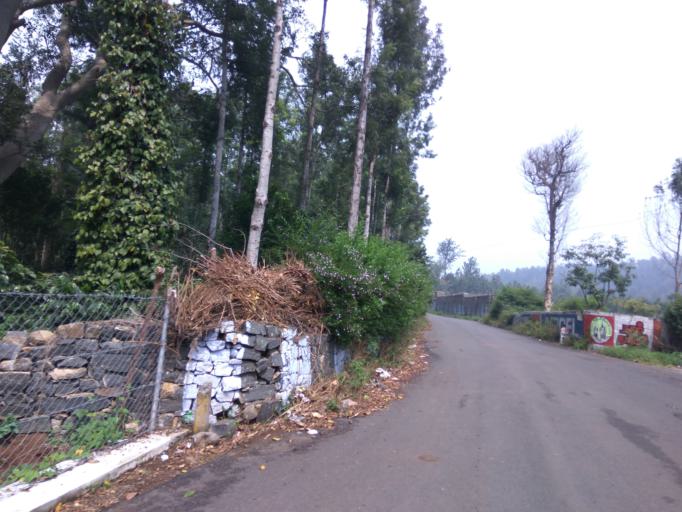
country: IN
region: Tamil Nadu
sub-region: Salem
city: Salem
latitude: 11.7707
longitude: 78.2344
